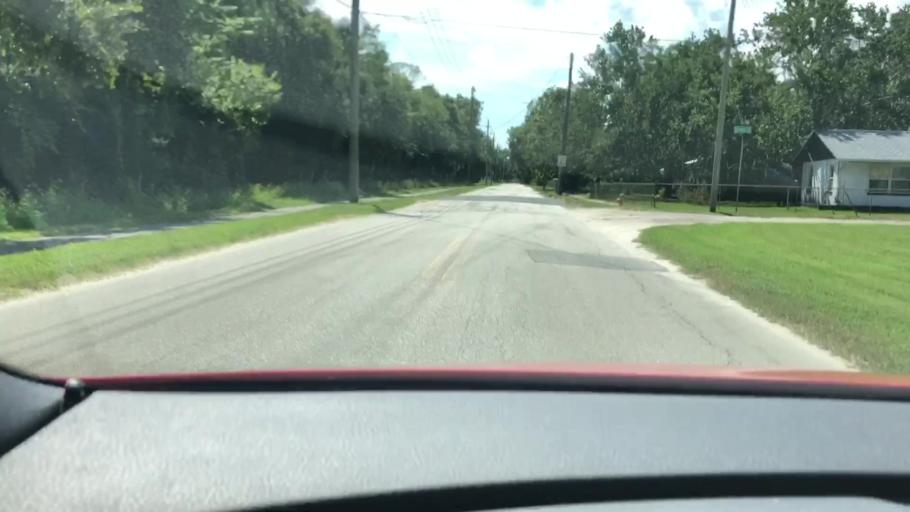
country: US
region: Florida
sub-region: Volusia County
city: New Smyrna Beach
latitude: 29.0130
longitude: -80.9264
